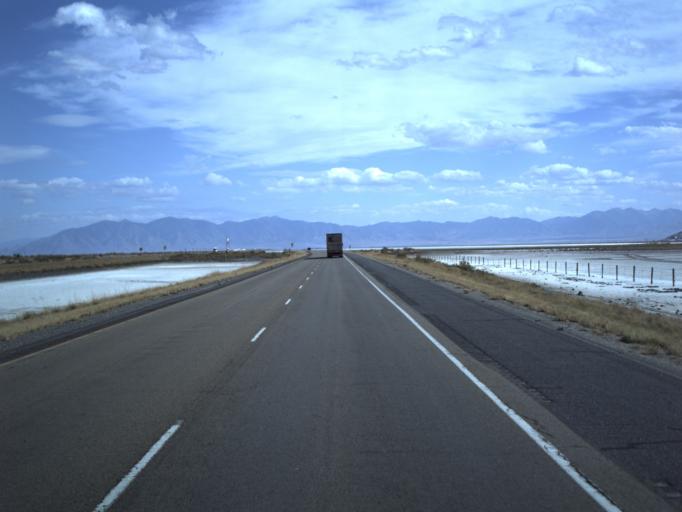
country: US
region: Utah
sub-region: Tooele County
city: Grantsville
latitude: 40.7412
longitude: -112.6274
